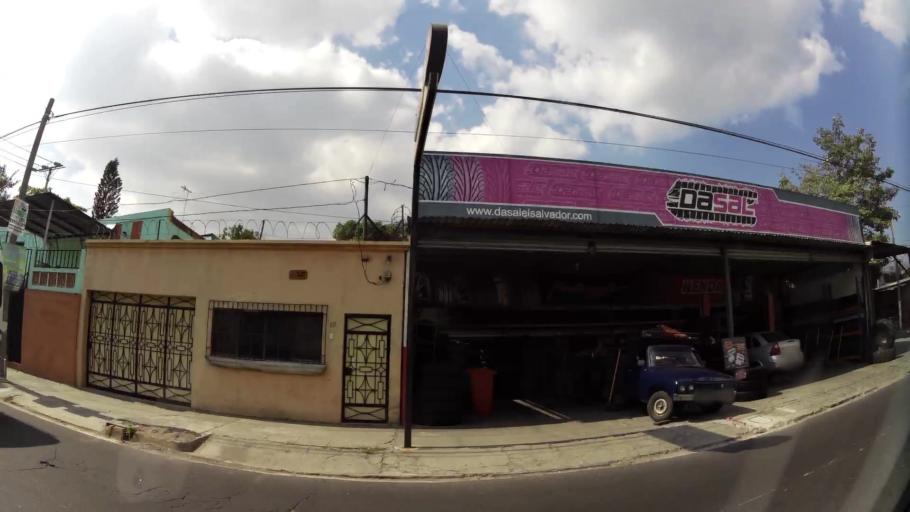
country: SV
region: San Salvador
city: Delgado
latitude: 13.7130
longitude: -89.1714
